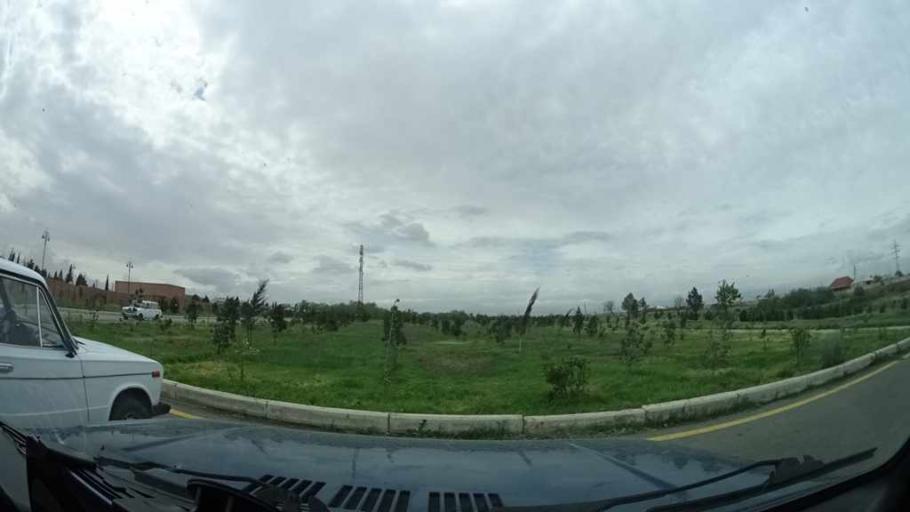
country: AZ
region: Samux
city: Samux
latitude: 40.7132
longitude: 46.4198
